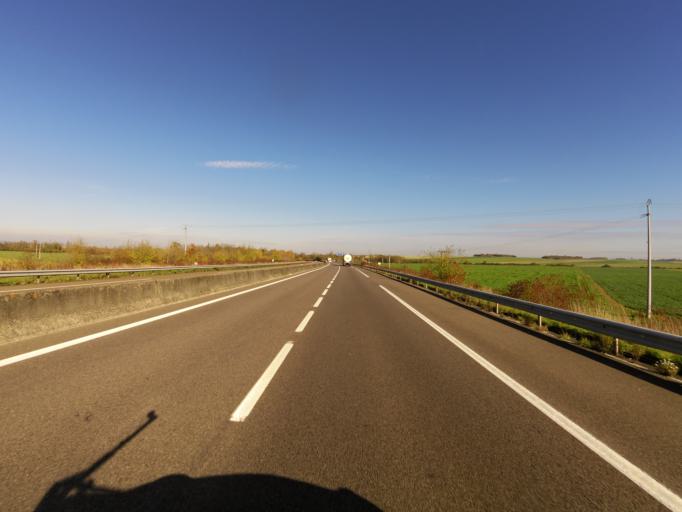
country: FR
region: Champagne-Ardenne
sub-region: Departement de la Marne
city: Fagnieres
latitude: 49.0013
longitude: 4.2982
